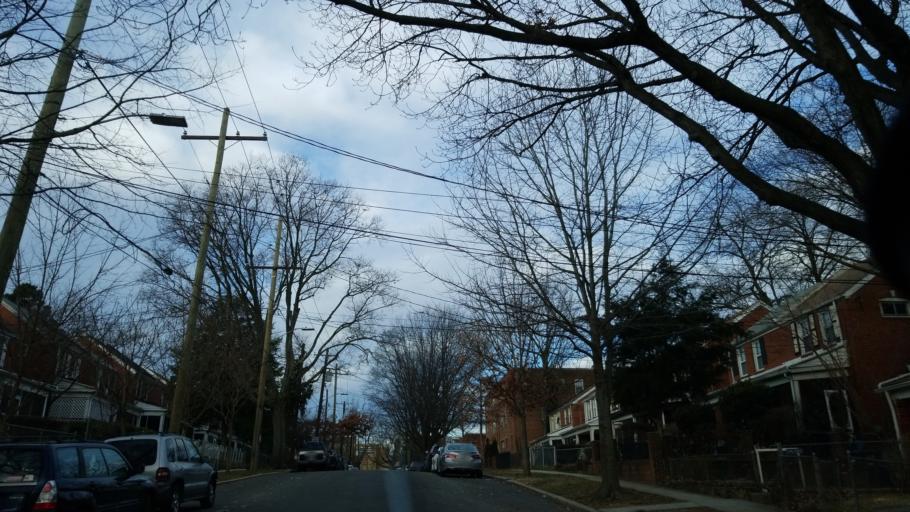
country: US
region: Maryland
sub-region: Prince George's County
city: Glassmanor
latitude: 38.8252
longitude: -77.0100
